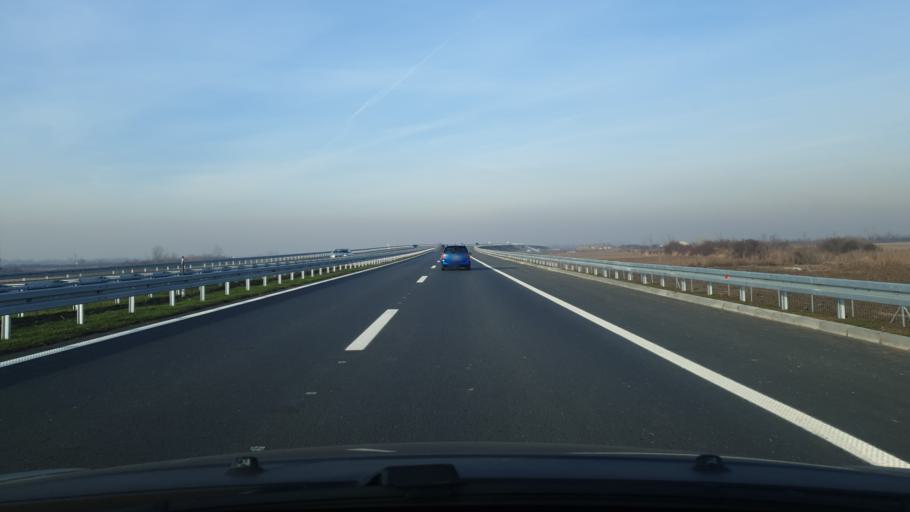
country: RS
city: Boljevci
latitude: 44.7114
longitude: 20.2599
